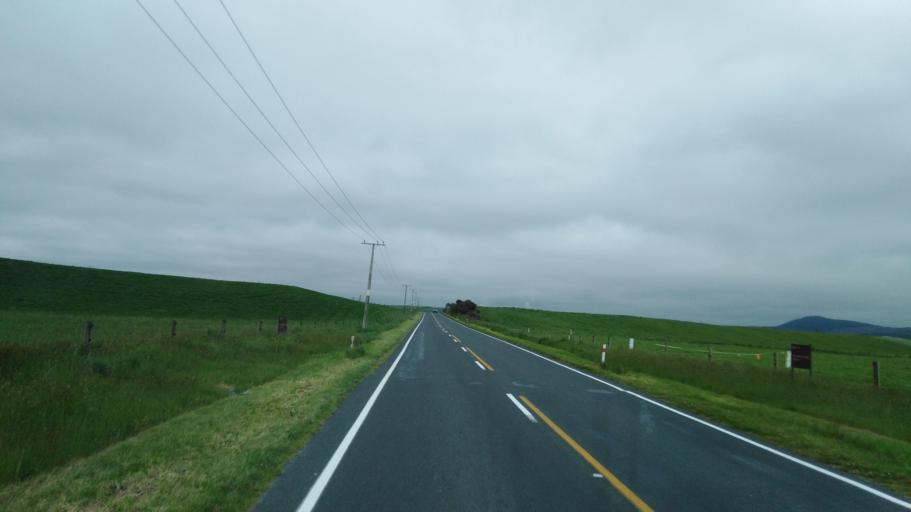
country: NZ
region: Waikato
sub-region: Taupo District
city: Taupo
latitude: -38.6159
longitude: 176.2523
